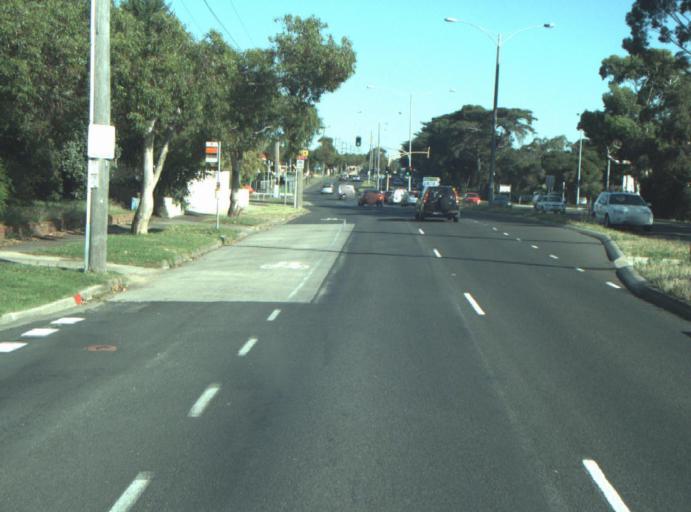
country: AU
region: Victoria
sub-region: Greater Geelong
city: Geelong West
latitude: -38.1280
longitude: 144.3402
